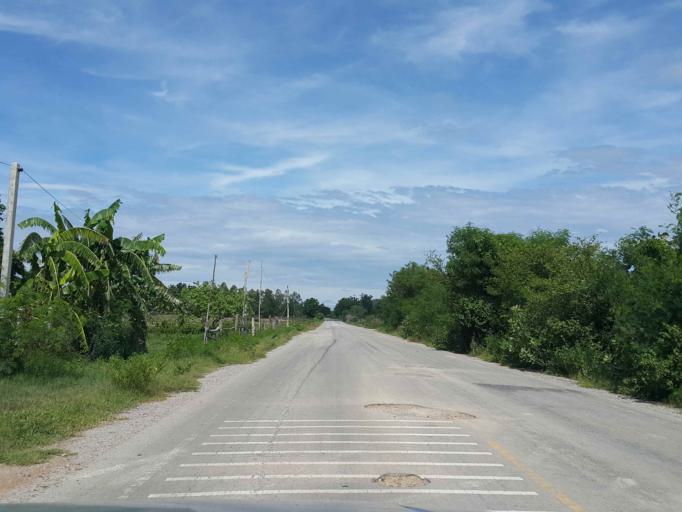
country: TH
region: Sukhothai
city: Ban Dan Lan Hoi
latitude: 17.1126
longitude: 99.5057
